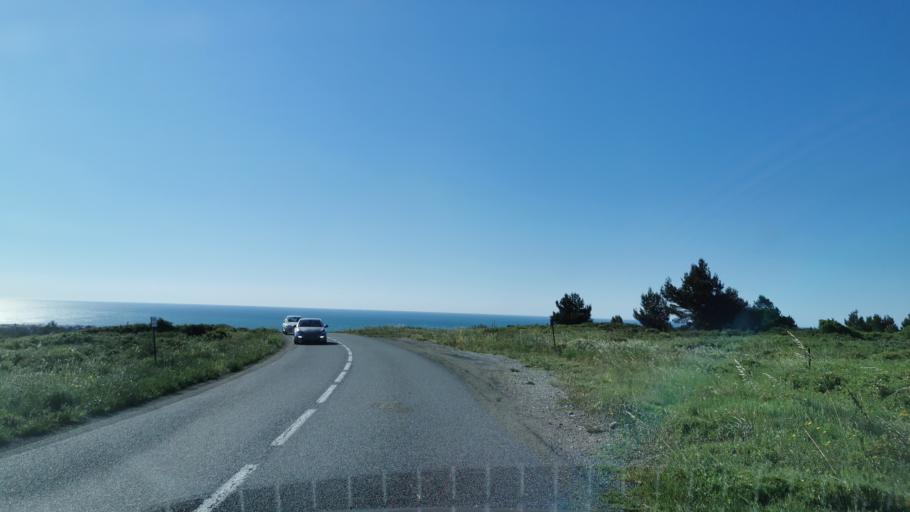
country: FR
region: Languedoc-Roussillon
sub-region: Departement de l'Aude
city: Armissan
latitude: 43.1620
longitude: 3.1360
